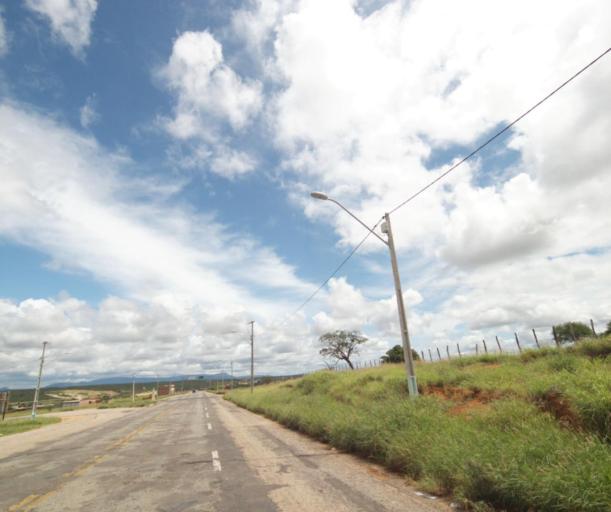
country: BR
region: Bahia
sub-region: Tanhacu
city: Tanhacu
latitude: -14.1635
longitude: -41.2055
